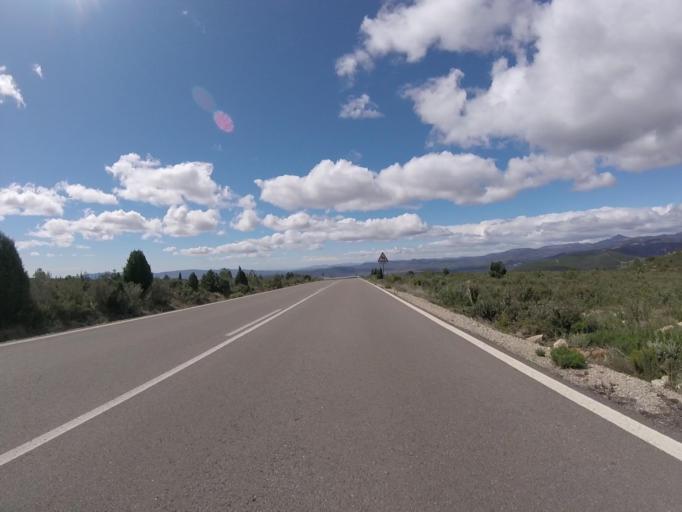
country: ES
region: Valencia
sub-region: Provincia de Castello
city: Culla
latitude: 40.3020
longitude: -0.1267
